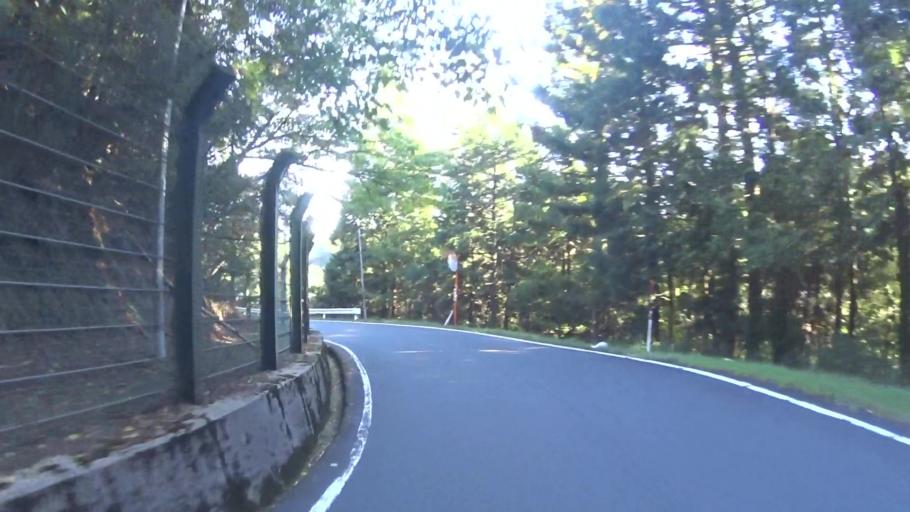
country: JP
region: Hyogo
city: Toyooka
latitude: 35.6122
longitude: 134.8815
